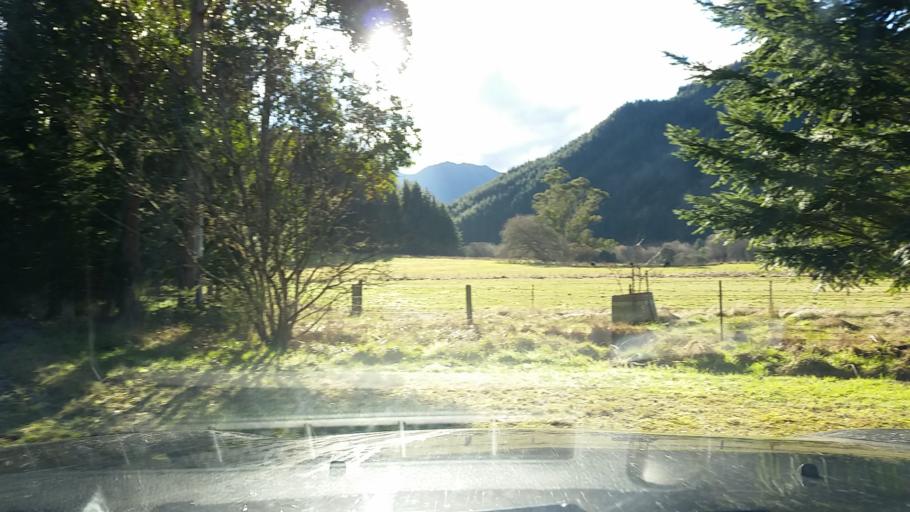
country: NZ
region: Nelson
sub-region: Nelson City
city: Nelson
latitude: -41.5512
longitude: 173.4194
